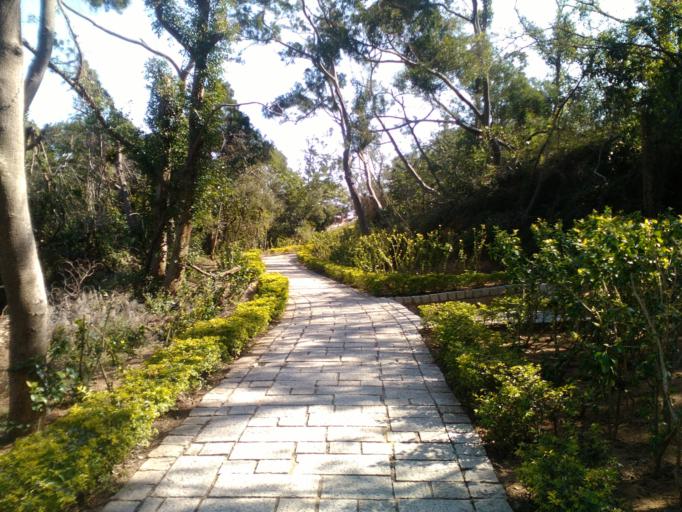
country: CN
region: Fujian
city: Shijing
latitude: 24.5059
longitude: 118.4370
